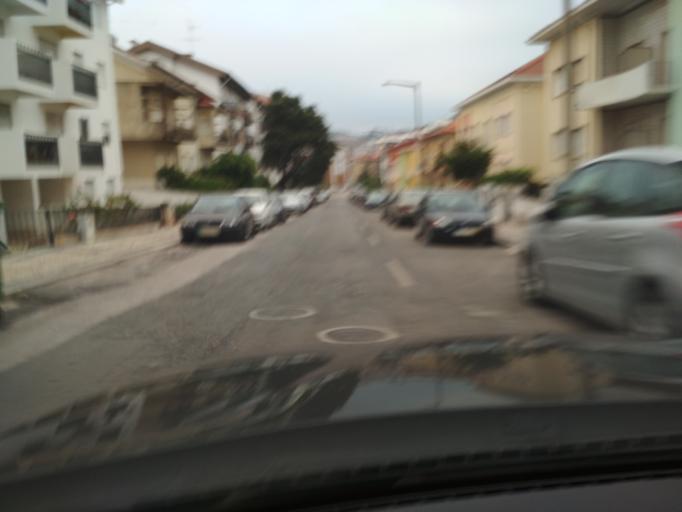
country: PT
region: Coimbra
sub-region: Coimbra
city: Coimbra
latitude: 40.1971
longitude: -8.4093
